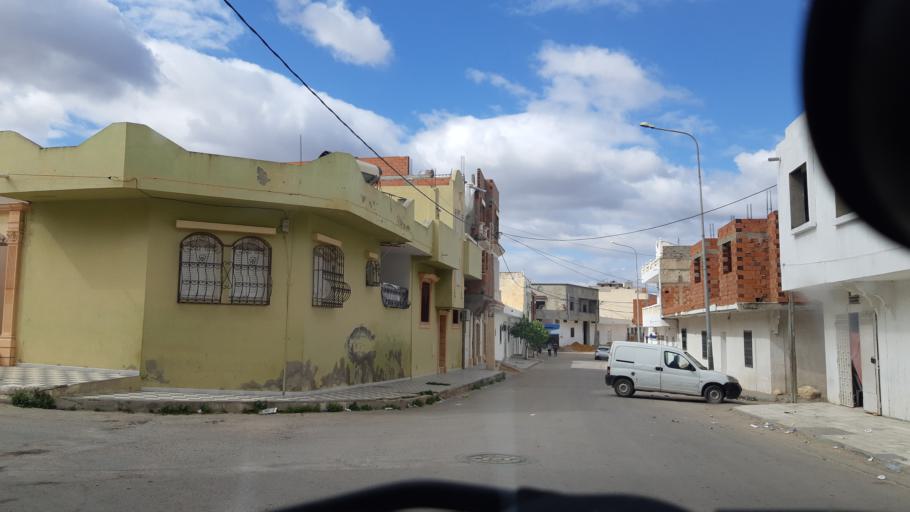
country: TN
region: Susah
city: Akouda
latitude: 35.8702
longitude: 10.5233
